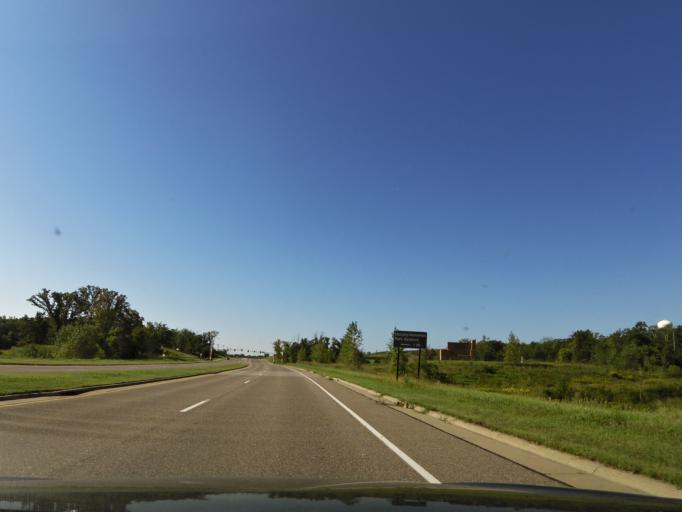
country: US
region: Minnesota
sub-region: Scott County
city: Prior Lake
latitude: 44.7275
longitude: -93.3723
